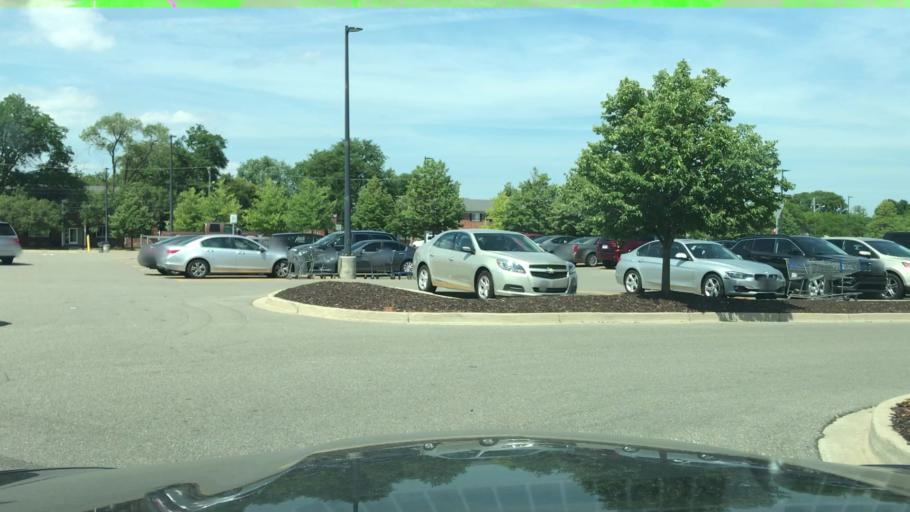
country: US
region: Michigan
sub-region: Oakland County
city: Madison Heights
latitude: 42.5216
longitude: -83.1056
